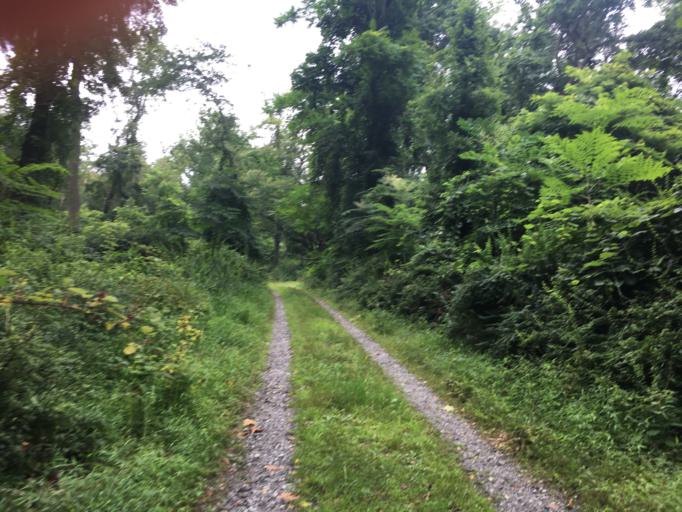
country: US
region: New York
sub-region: Orange County
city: Fort Montgomery
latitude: 41.2992
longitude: -73.9917
